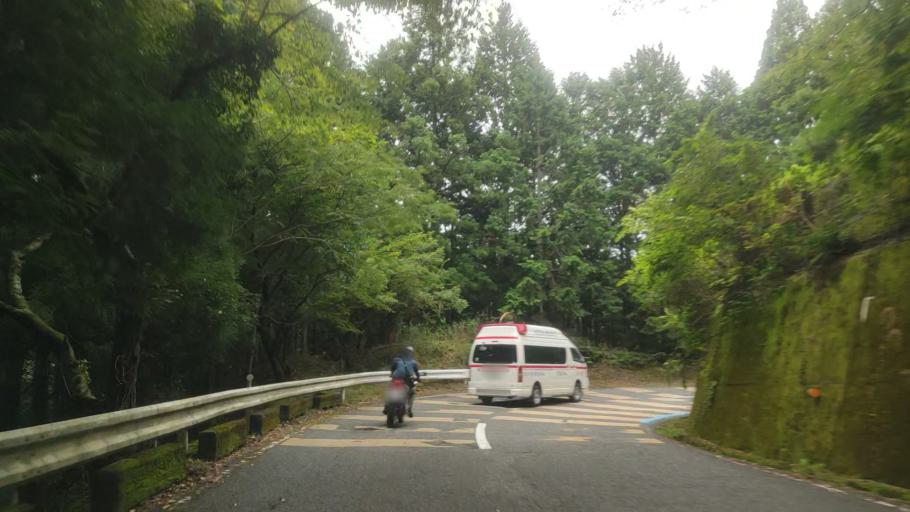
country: JP
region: Wakayama
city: Koya
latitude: 34.2224
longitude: 135.5375
